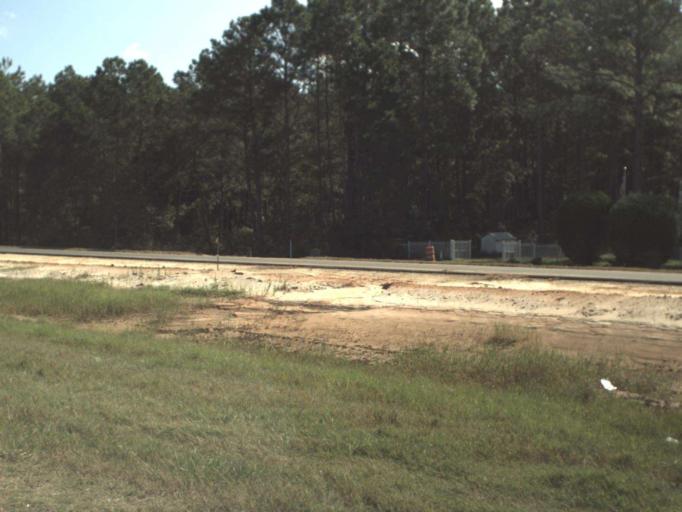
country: US
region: Florida
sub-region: Walton County
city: Freeport
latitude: 30.4387
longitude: -86.1493
